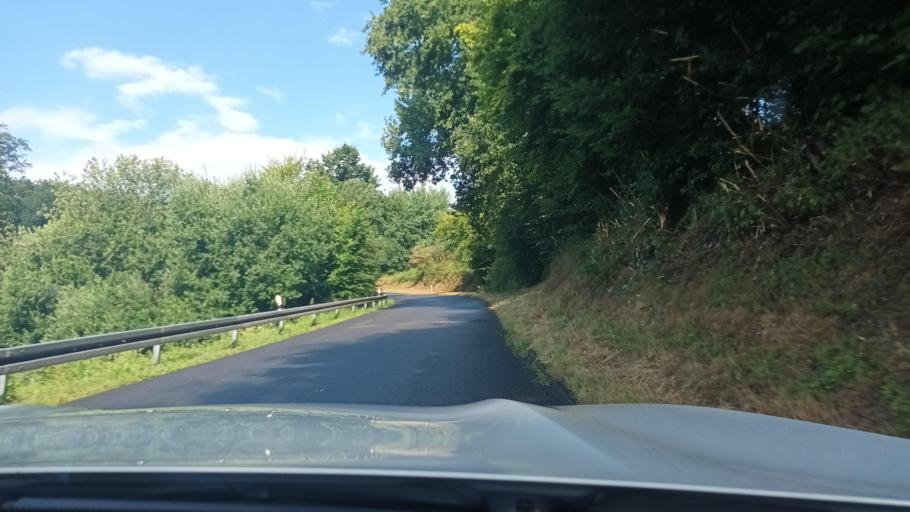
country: DE
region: North Rhine-Westphalia
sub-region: Regierungsbezirk Koln
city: Hennef
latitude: 50.7946
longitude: 7.3127
